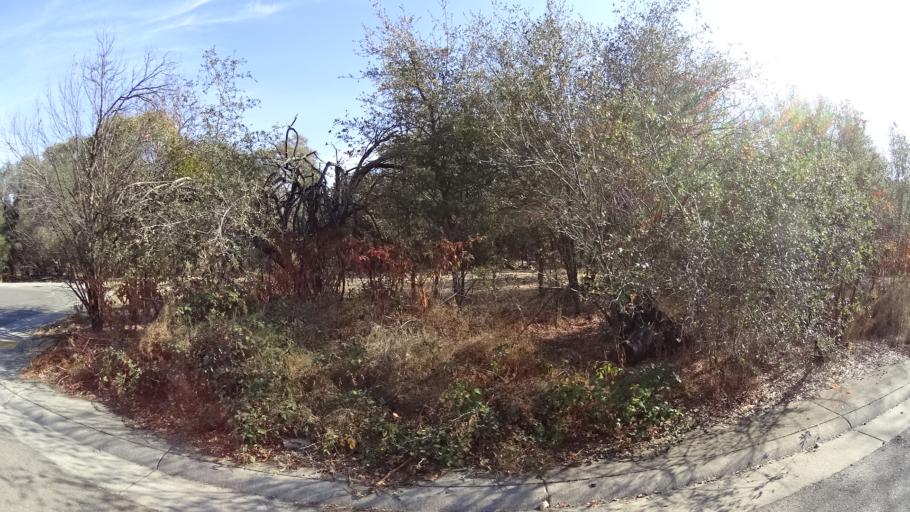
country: US
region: California
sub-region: Sacramento County
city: Citrus Heights
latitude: 38.6863
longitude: -121.2928
